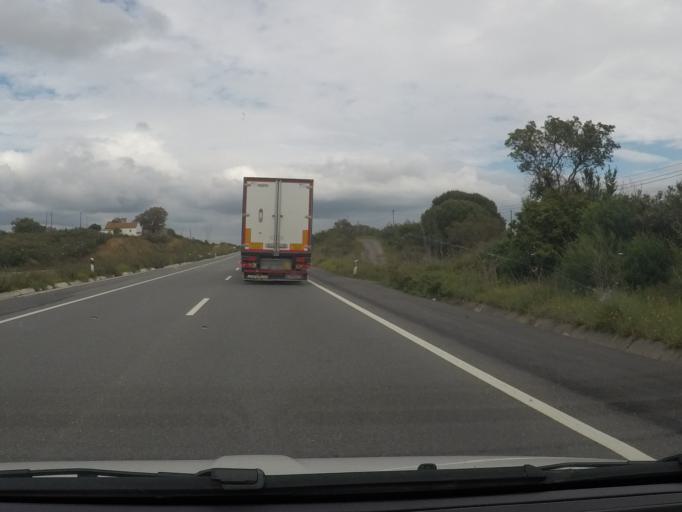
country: PT
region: Setubal
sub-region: Santiago do Cacem
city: Santiago do Cacem
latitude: 38.0708
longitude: -8.6659
